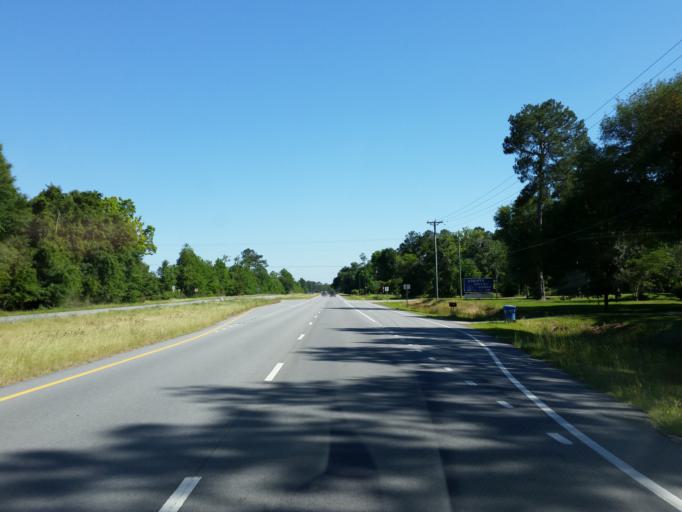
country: US
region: Georgia
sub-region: Lowndes County
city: Valdosta
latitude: 30.7118
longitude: -83.2141
